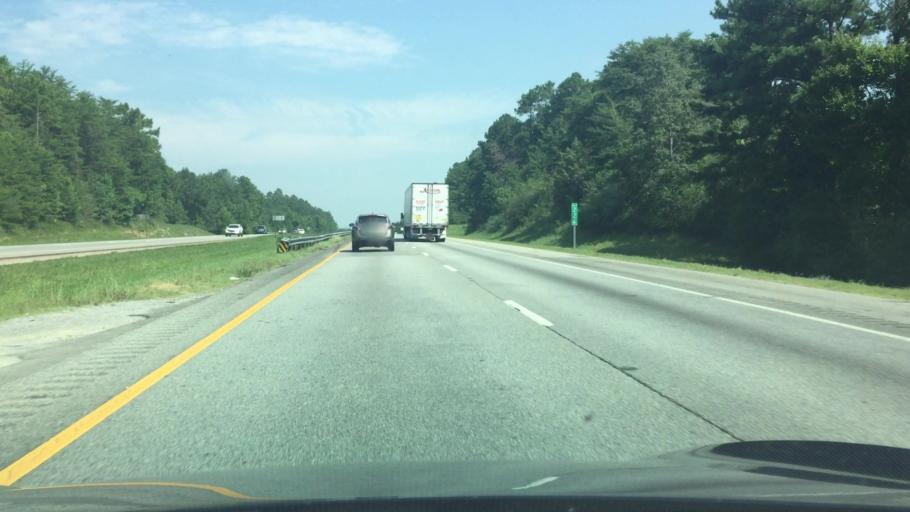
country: US
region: Alabama
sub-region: Shelby County
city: Calera
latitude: 33.0699
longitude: -86.7302
